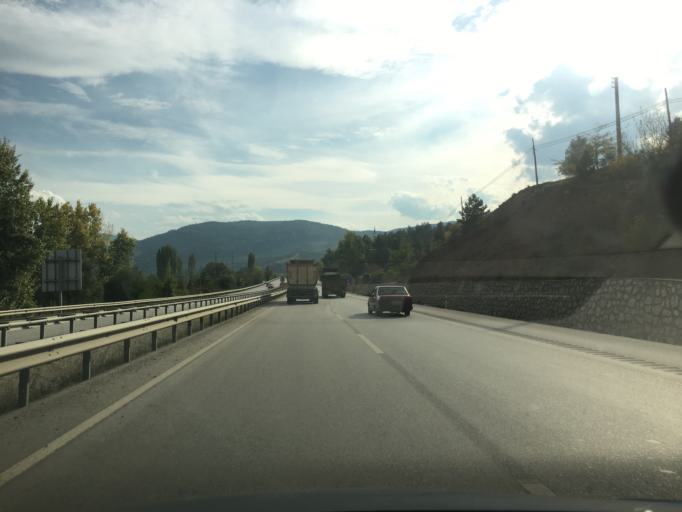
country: TR
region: Karabuk
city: Karabuk
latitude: 41.1158
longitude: 32.6719
